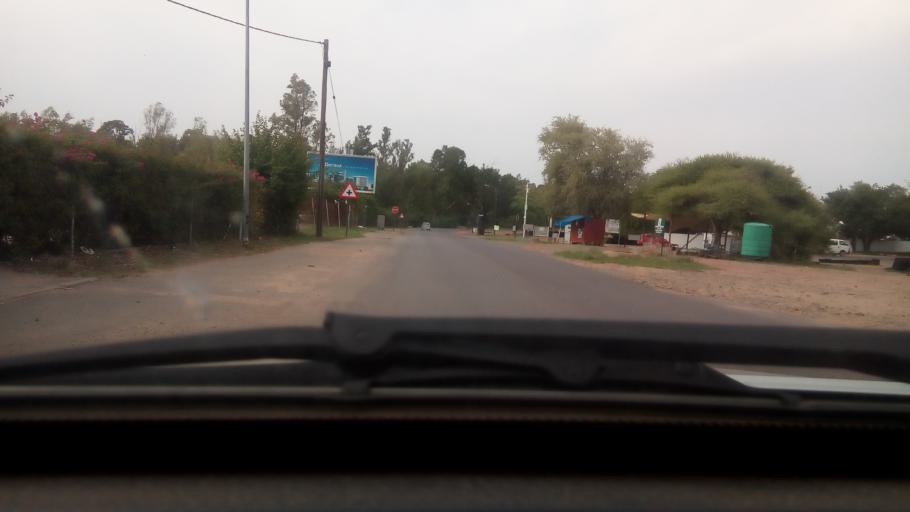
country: BW
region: South East
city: Gaborone
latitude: -24.6682
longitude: 25.9415
